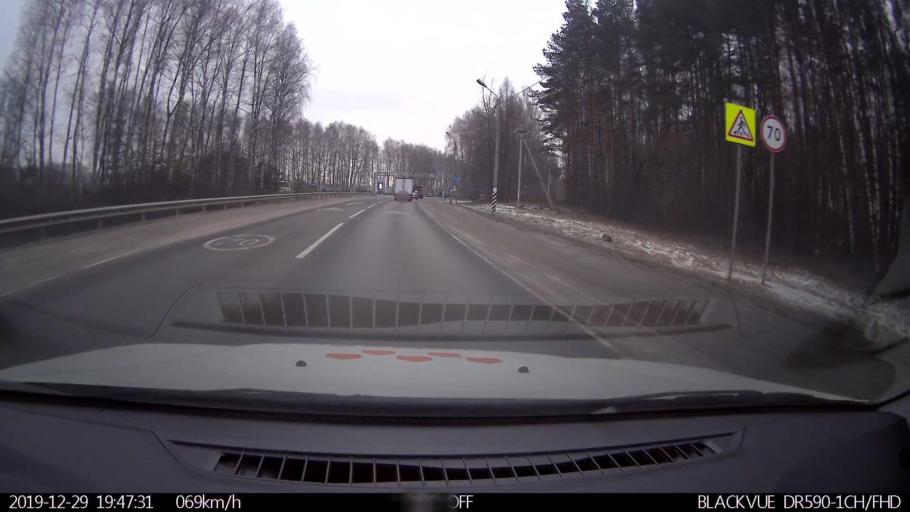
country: RU
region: Nizjnij Novgorod
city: Neklyudovo
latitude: 56.3929
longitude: 44.0092
